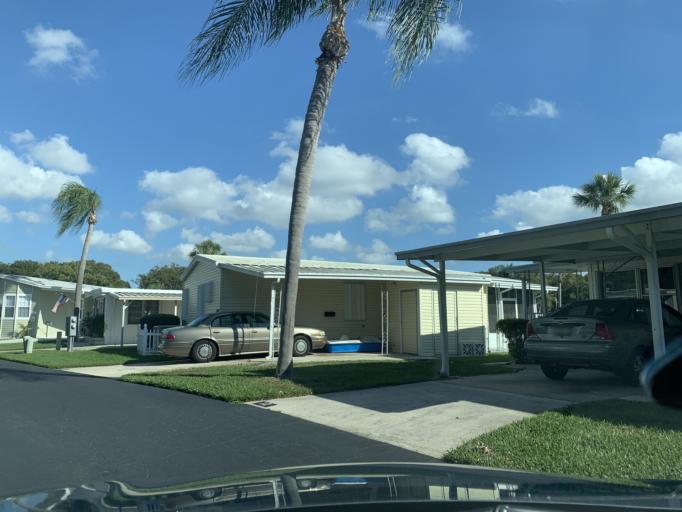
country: US
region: Florida
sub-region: Pinellas County
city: Largo
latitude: 27.9249
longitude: -82.7934
